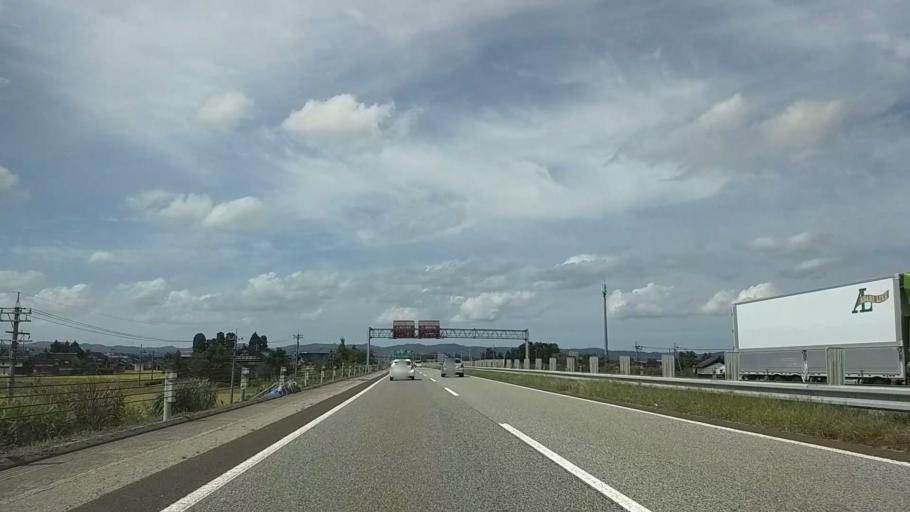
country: JP
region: Toyama
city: Nanto-shi
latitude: 36.6272
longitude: 136.9217
